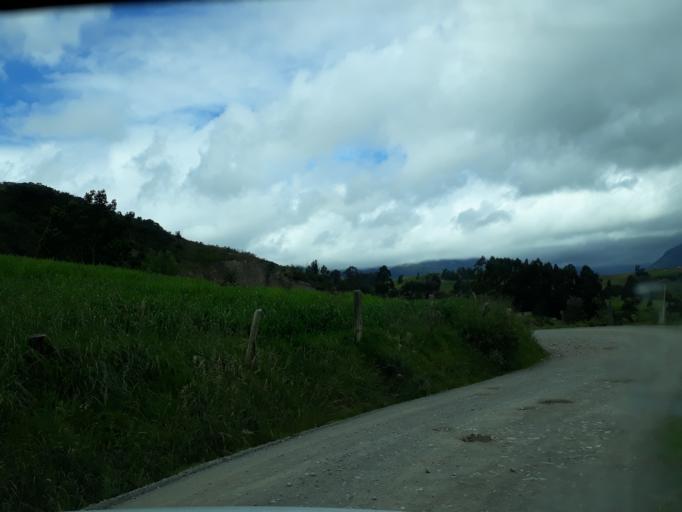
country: CO
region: Cundinamarca
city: Carmen de Carupa
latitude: 5.3112
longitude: -73.8970
